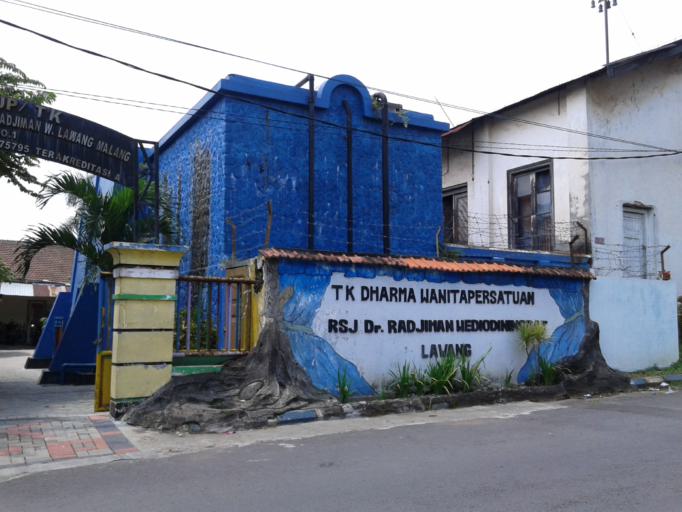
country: ID
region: East Java
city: Lawang
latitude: -7.8209
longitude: 112.7158
